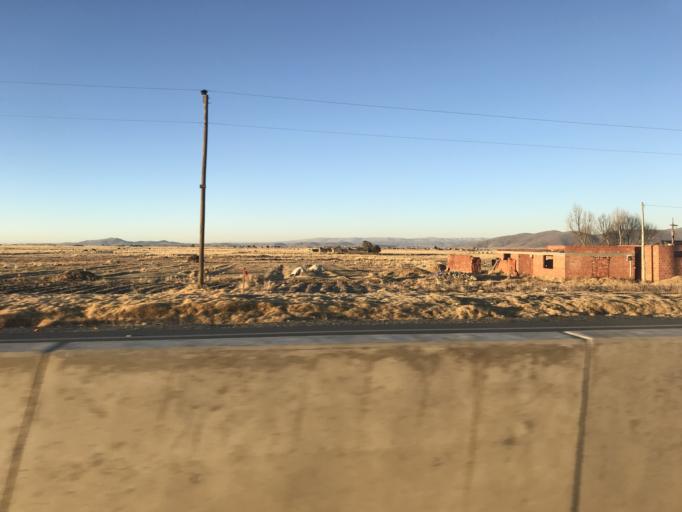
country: BO
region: La Paz
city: Batallas
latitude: -16.2993
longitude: -68.5061
